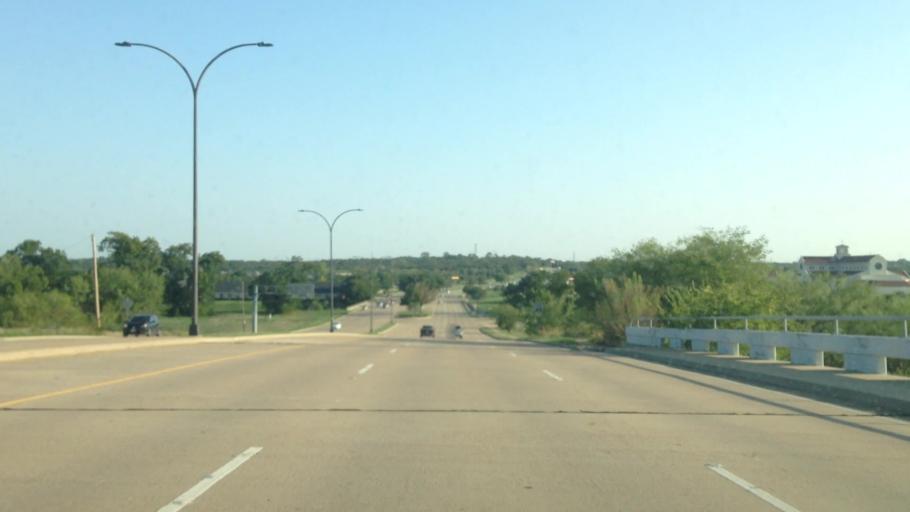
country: US
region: Texas
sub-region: Tarrant County
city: Pantego
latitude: 32.7303
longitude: -97.1814
